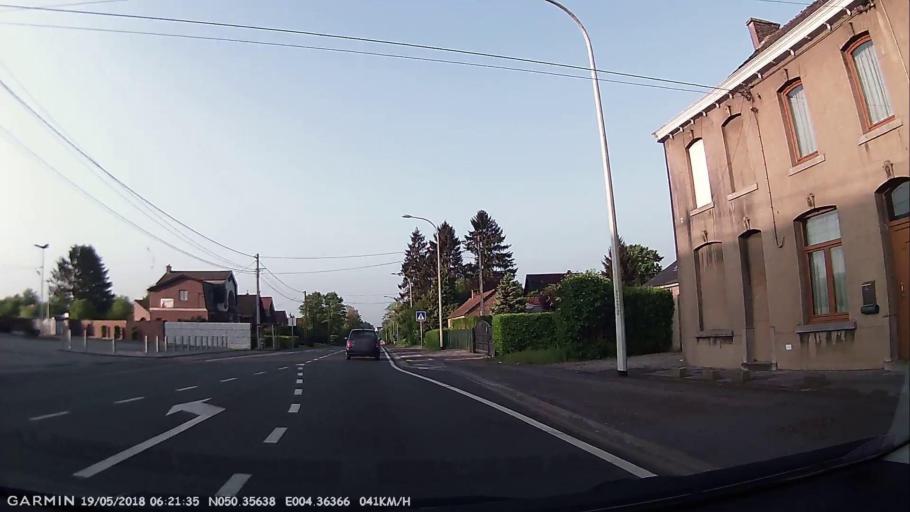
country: BE
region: Wallonia
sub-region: Province du Hainaut
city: Thuin
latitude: 50.3563
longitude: 4.3637
